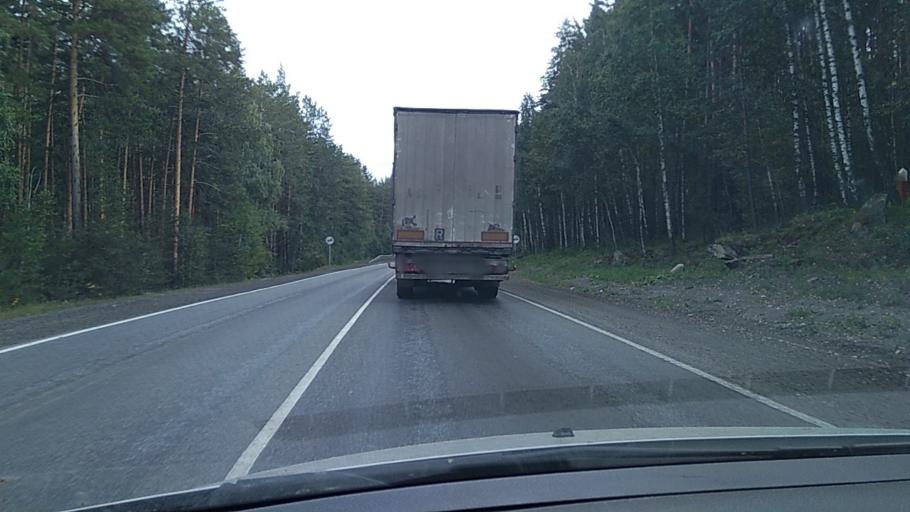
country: RU
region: Chelyabinsk
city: Miass
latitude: 54.9443
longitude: 60.1097
